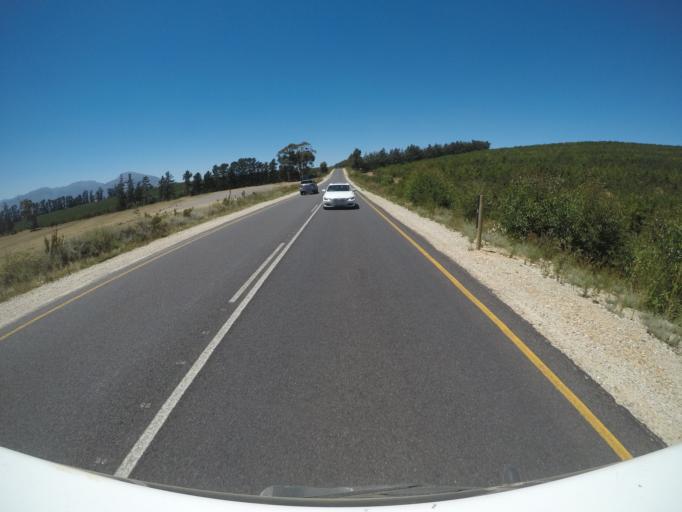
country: ZA
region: Western Cape
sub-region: Overberg District Municipality
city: Grabouw
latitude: -34.0680
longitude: 19.1243
